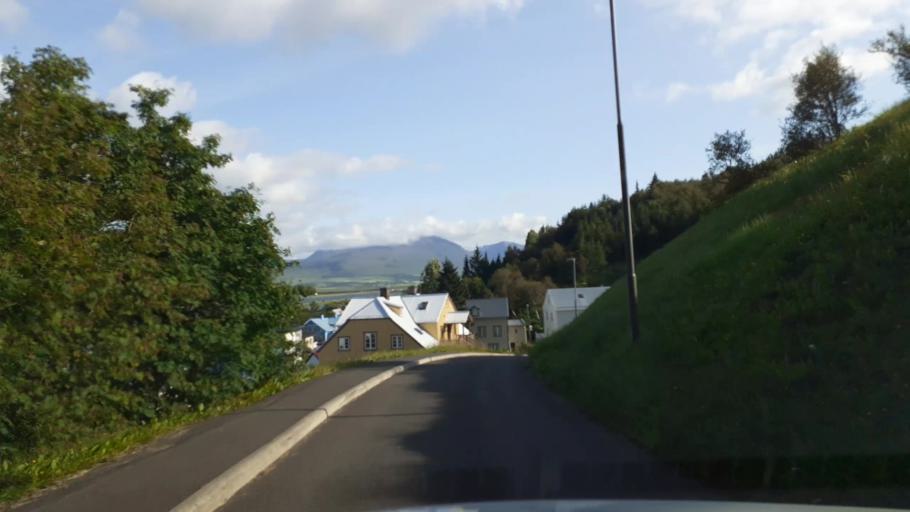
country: IS
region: Northeast
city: Akureyri
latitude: 65.6729
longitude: -18.0883
